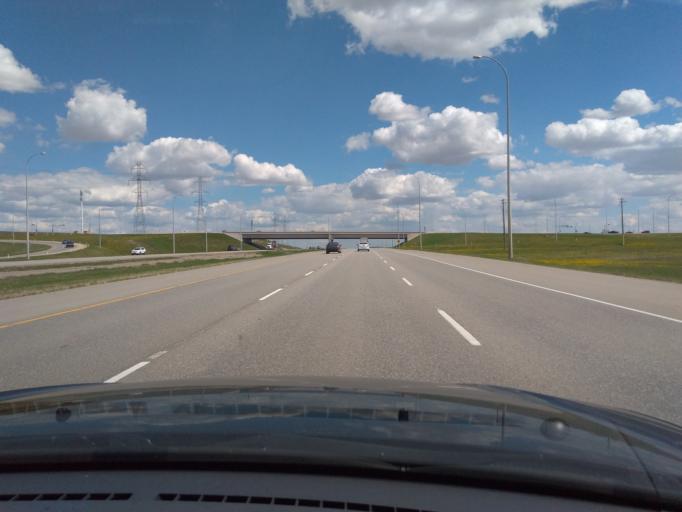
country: CA
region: Alberta
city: Calgary
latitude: 51.1738
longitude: -114.0739
